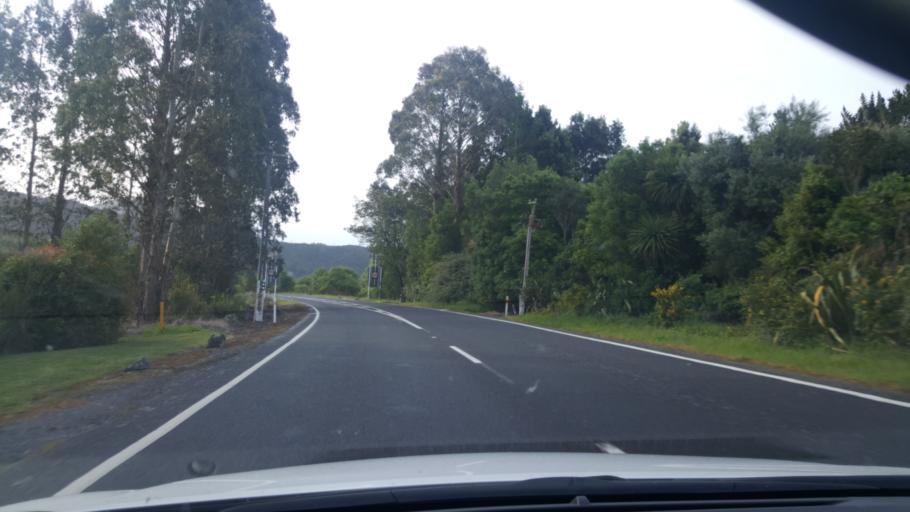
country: NZ
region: Waikato
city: Turangi
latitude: -38.9607
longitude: 175.7639
